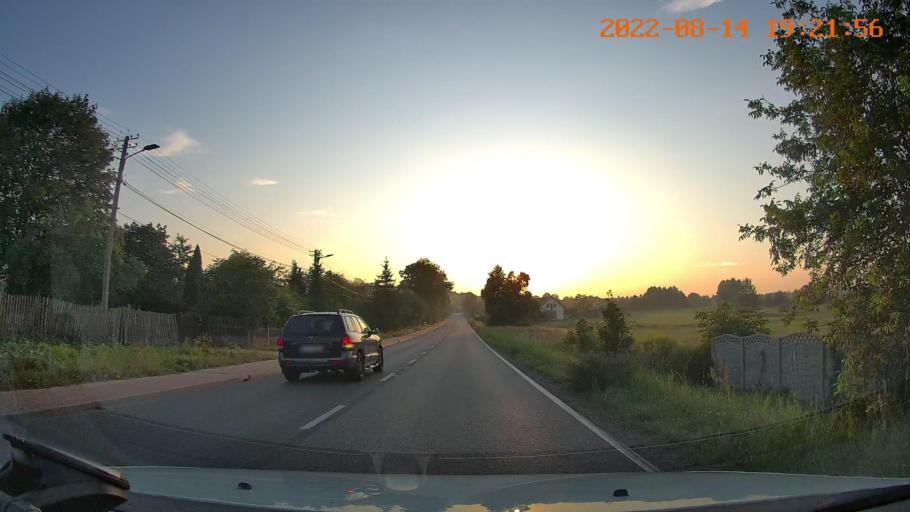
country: PL
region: Swietokrzyskie
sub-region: Powiat kielecki
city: Piekoszow
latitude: 50.8596
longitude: 20.4888
